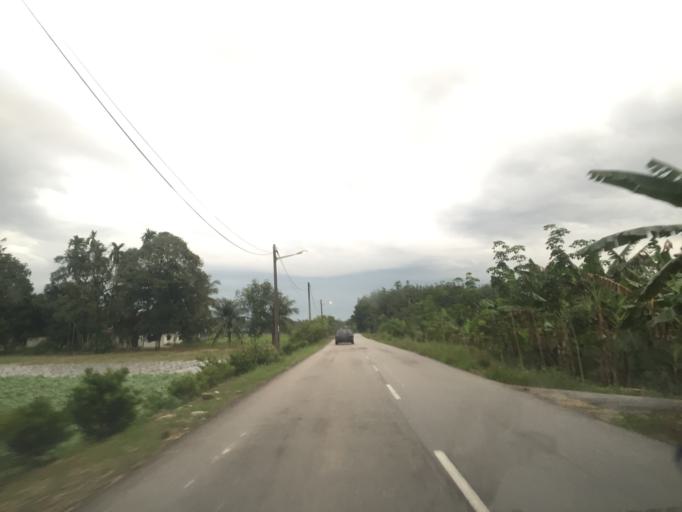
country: MY
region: Penang
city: Tasek Glugor
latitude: 5.5362
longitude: 100.5155
